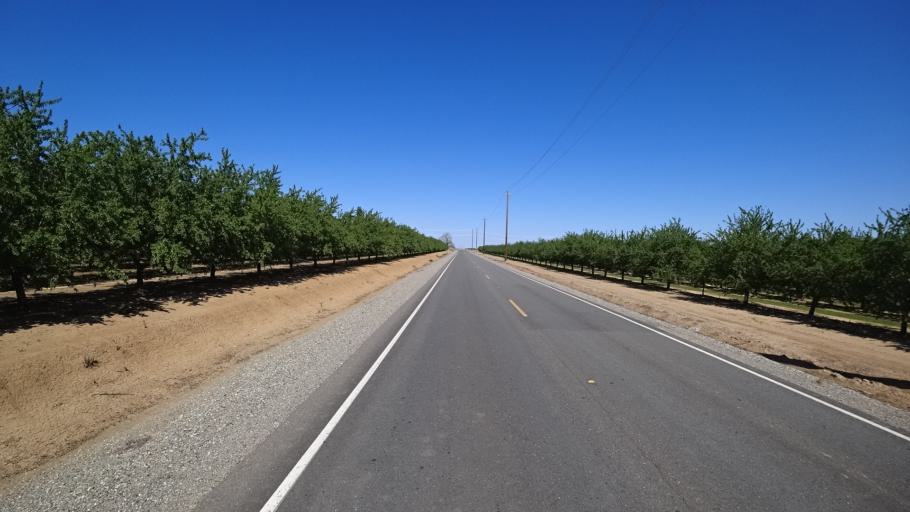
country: US
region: California
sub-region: Glenn County
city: Willows
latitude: 39.5360
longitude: -122.2494
